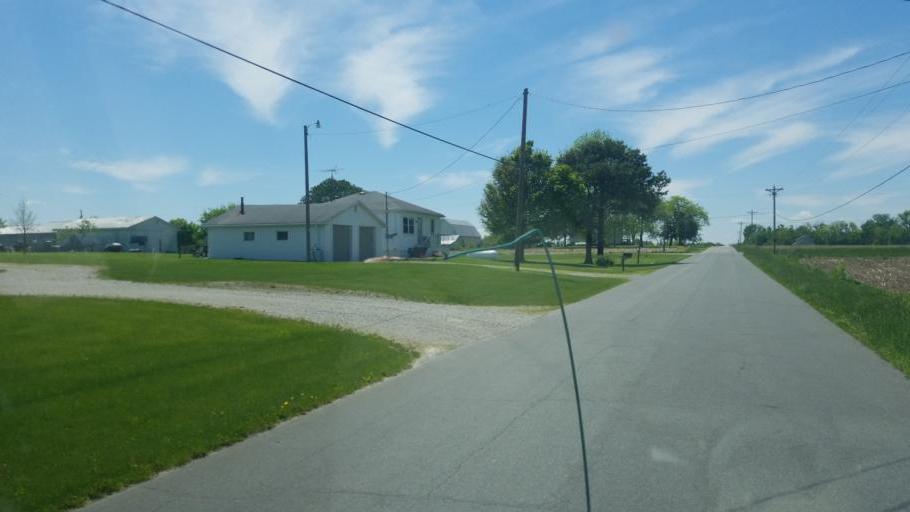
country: US
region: Ohio
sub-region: Huron County
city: Willard
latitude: 41.0835
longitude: -82.7662
